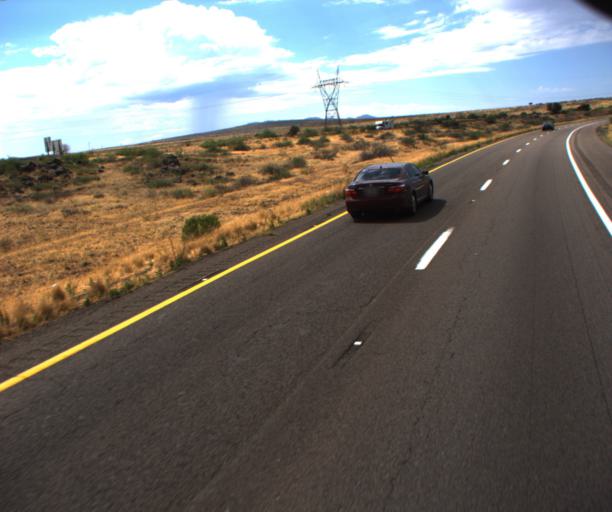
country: US
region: Arizona
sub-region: Yavapai County
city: Cordes Lakes
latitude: 34.2205
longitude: -112.1117
